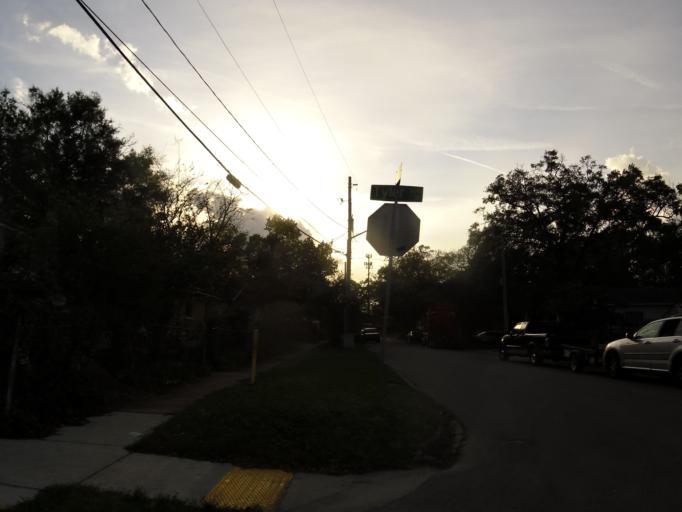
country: US
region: Florida
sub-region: Duval County
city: Jacksonville
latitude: 30.3450
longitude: -81.6821
